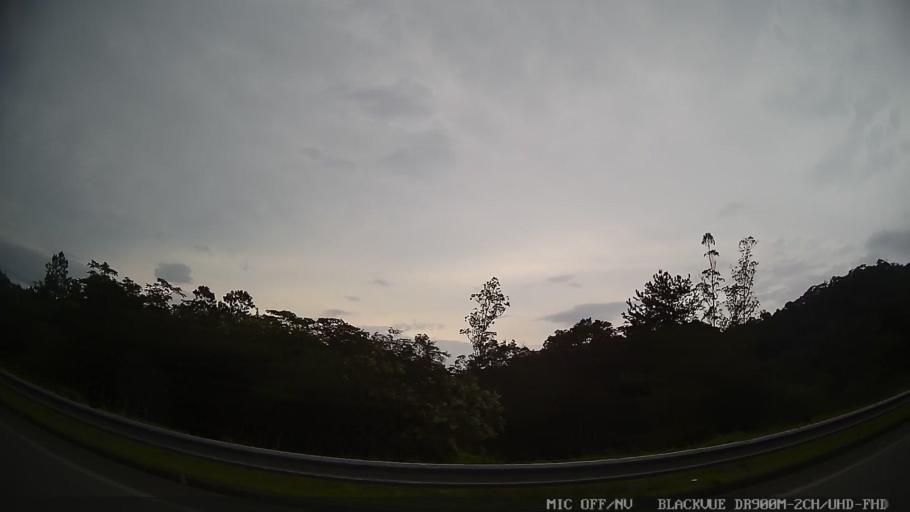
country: BR
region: Sao Paulo
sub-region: Caraguatatuba
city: Caraguatatuba
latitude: -23.5707
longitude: -45.4909
